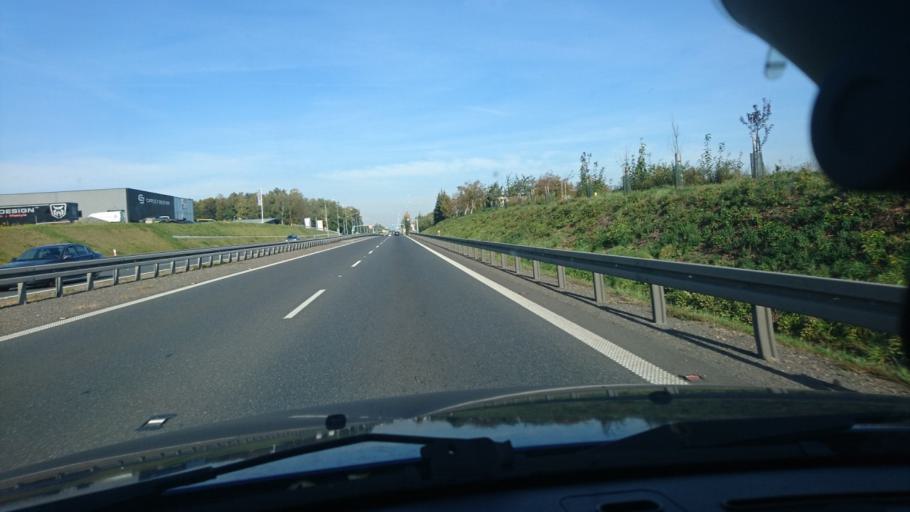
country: PL
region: Silesian Voivodeship
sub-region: Powiat bielski
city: Mazancowice
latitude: 49.8663
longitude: 19.0113
